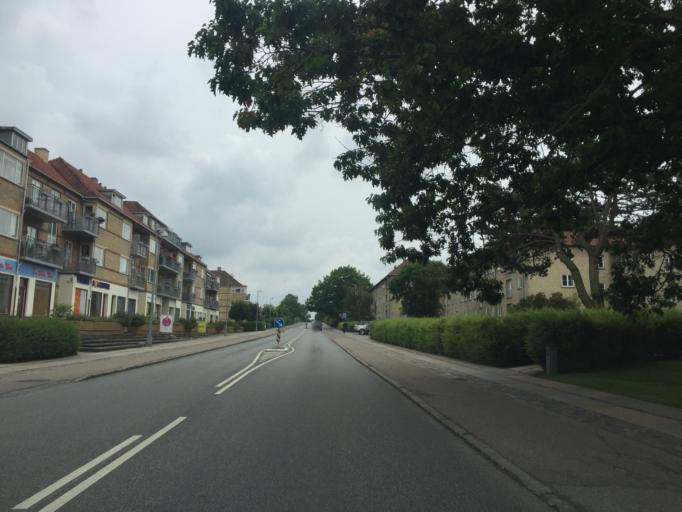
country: DK
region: Capital Region
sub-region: Rudersdal Kommune
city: Holte
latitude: 55.7943
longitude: 12.4722
